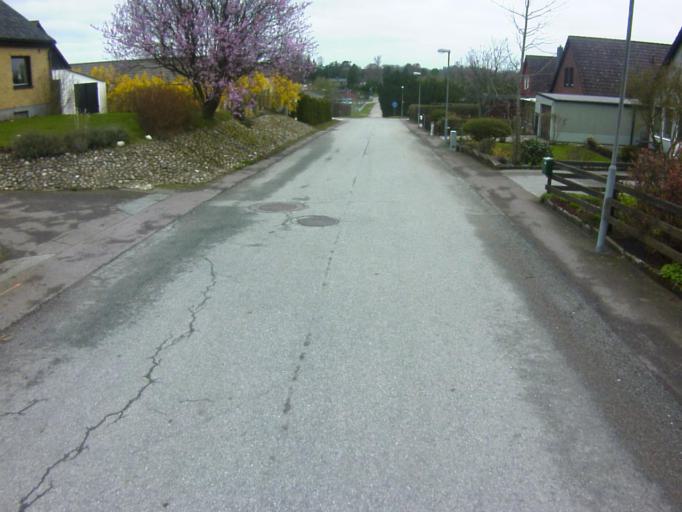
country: SE
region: Skane
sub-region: Kavlinge Kommun
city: Kaevlinge
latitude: 55.7685
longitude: 13.0843
